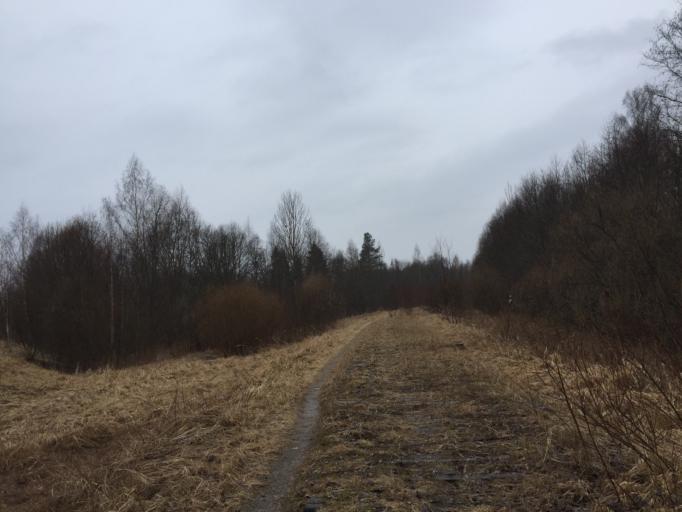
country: LV
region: Lielvarde
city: Lielvarde
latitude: 56.7261
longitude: 24.7807
